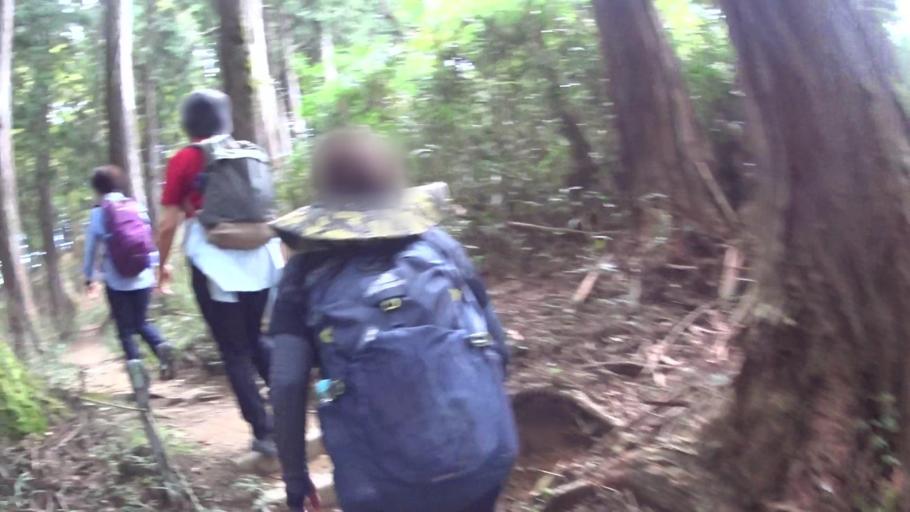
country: JP
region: Shiga Prefecture
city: Otsu-shi
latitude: 35.0792
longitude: 135.8376
